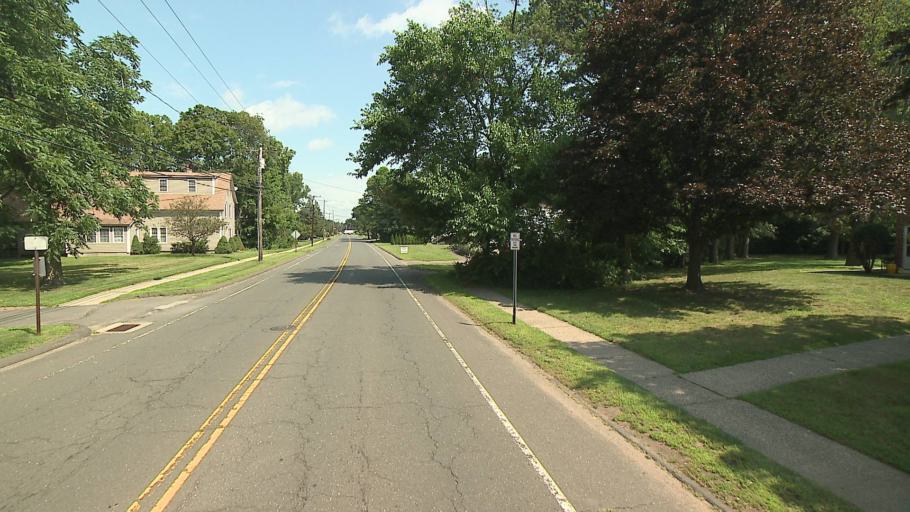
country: US
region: Connecticut
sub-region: Hartford County
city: Plainville
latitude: 41.6628
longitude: -72.8750
